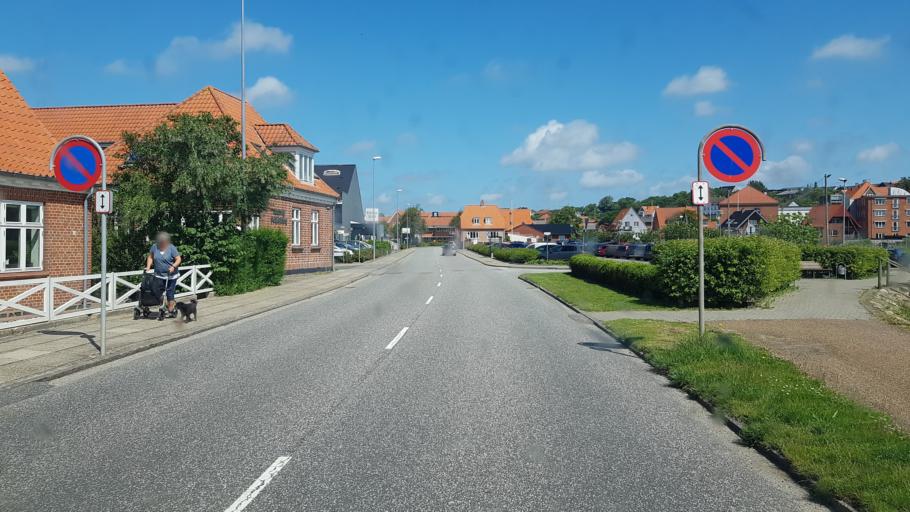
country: DK
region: Central Jutland
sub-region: Lemvig Kommune
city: Lemvig
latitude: 56.5475
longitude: 8.3131
